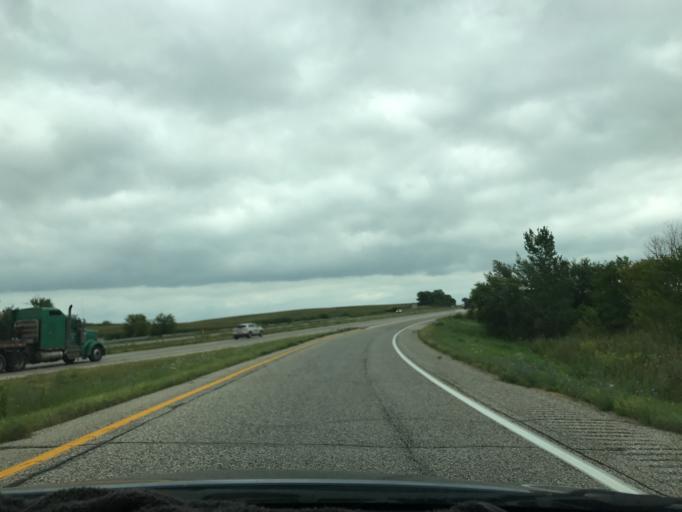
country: US
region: Iowa
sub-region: Scott County
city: Bettendorf
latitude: 41.5957
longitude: -90.5228
